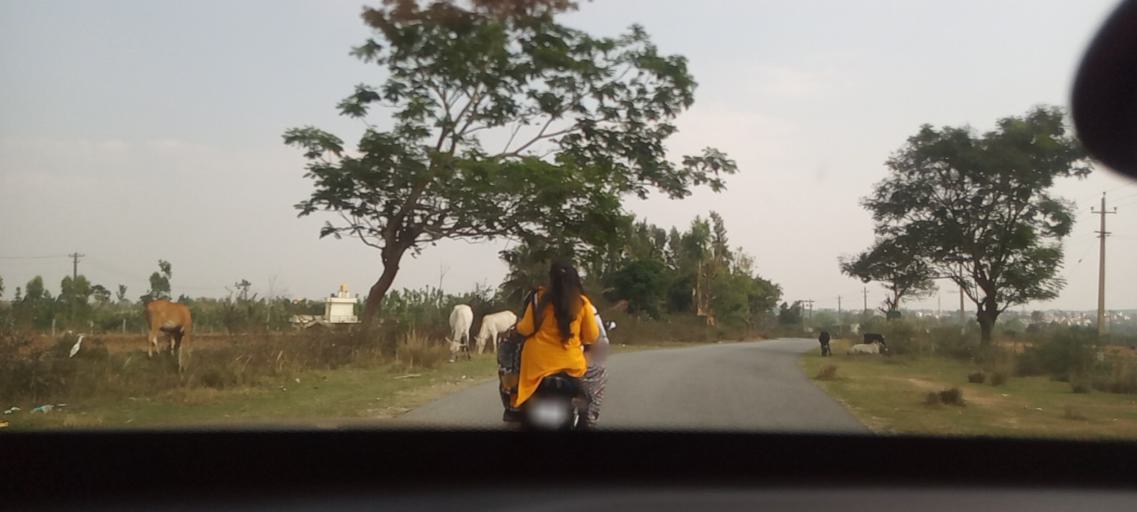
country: IN
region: Karnataka
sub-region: Hassan
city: Belur
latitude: 13.1779
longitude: 75.8470
